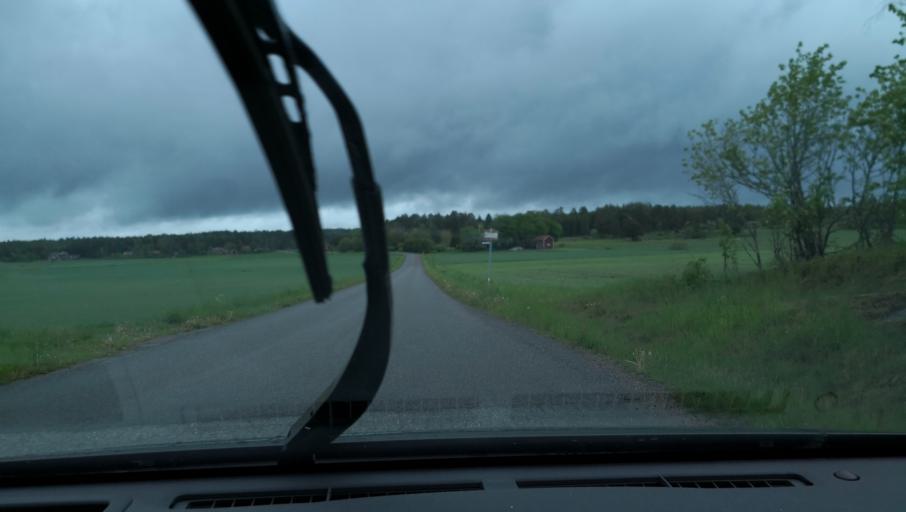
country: SE
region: Uppsala
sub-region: Enkopings Kommun
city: Orsundsbro
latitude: 59.8116
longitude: 17.3841
